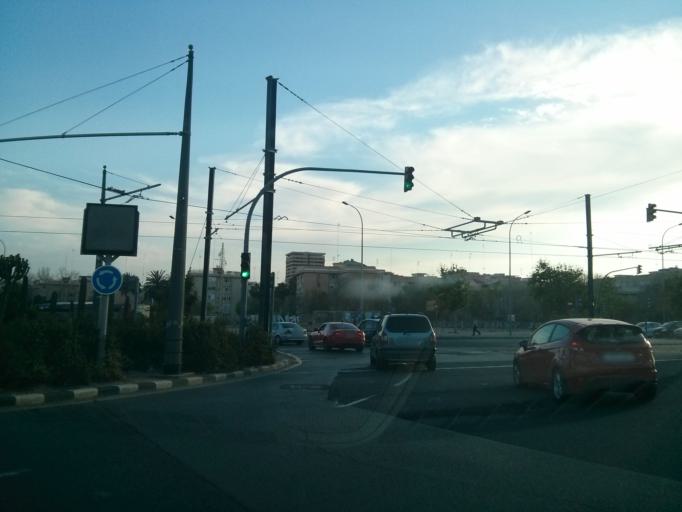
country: ES
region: Valencia
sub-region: Provincia de Valencia
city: Alboraya
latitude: 39.4767
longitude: -0.3334
